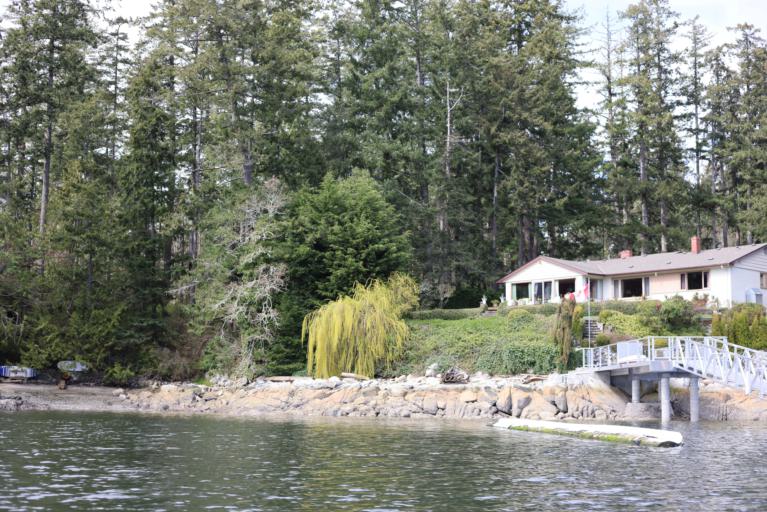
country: CA
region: British Columbia
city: North Saanich
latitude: 48.6274
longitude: -123.4762
